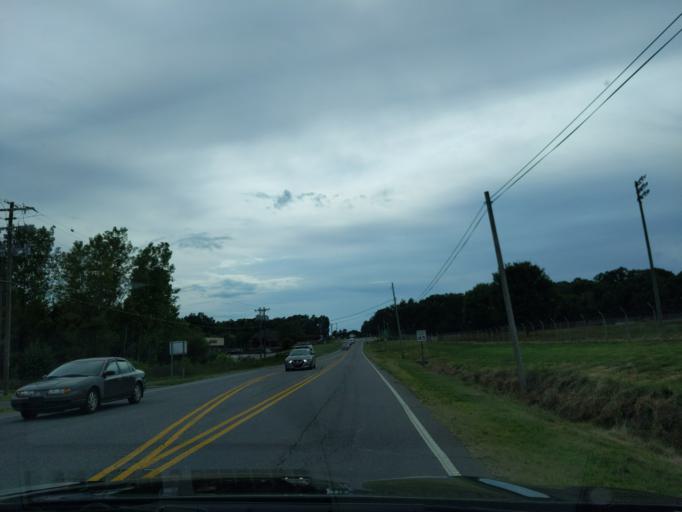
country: US
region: North Carolina
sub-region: Cabarrus County
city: Mount Pleasant
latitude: 35.4108
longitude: -80.4360
